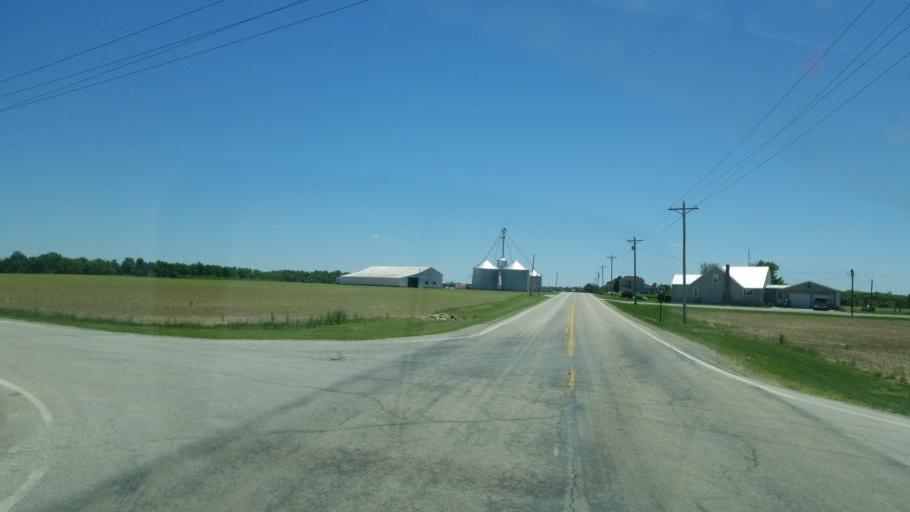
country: US
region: Ohio
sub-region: Darke County
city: Ansonia
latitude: 40.2650
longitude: -84.7004
